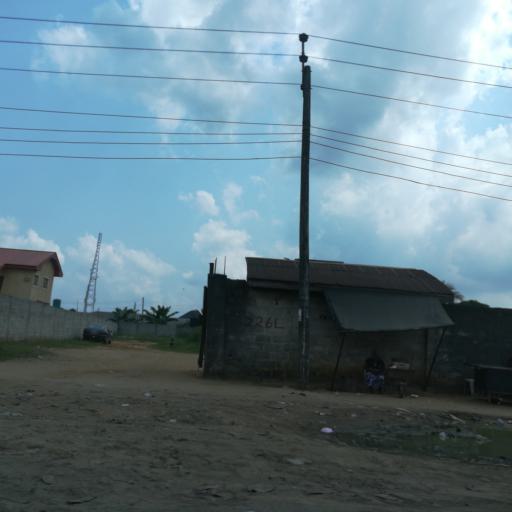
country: NG
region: Rivers
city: Okrika
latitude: 4.8244
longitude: 7.0919
